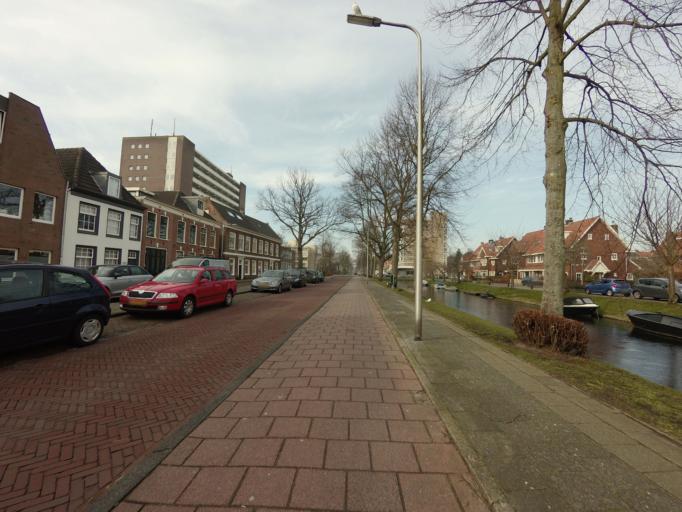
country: NL
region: North Holland
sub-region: Gemeente Heemstede
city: Heemstede
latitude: 52.3504
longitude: 4.6187
